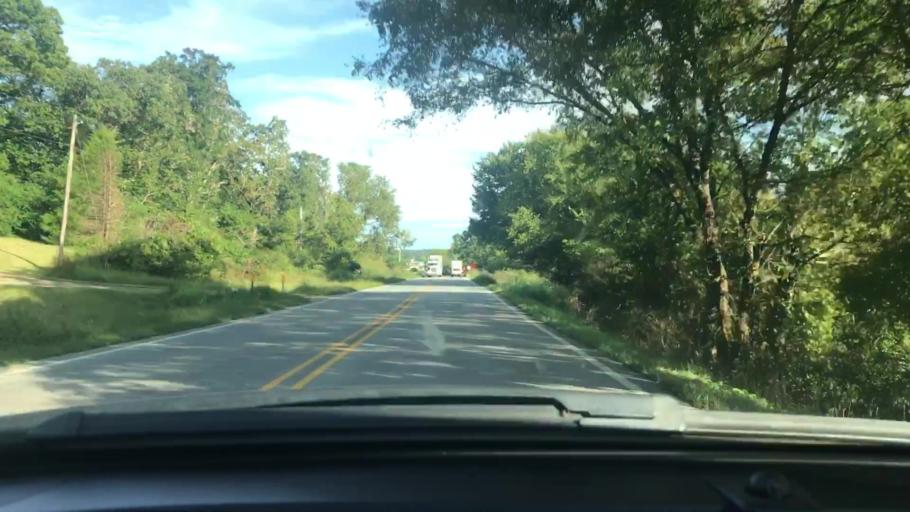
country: US
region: Arkansas
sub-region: Sharp County
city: Cherokee Village
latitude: 36.3065
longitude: -91.4534
